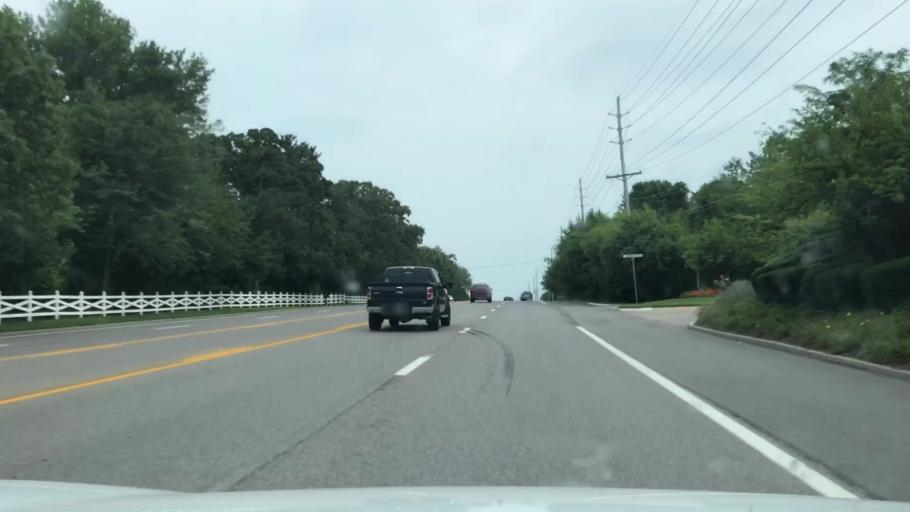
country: US
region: Missouri
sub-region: Saint Louis County
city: Clarkson Valley
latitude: 38.6113
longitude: -90.5858
